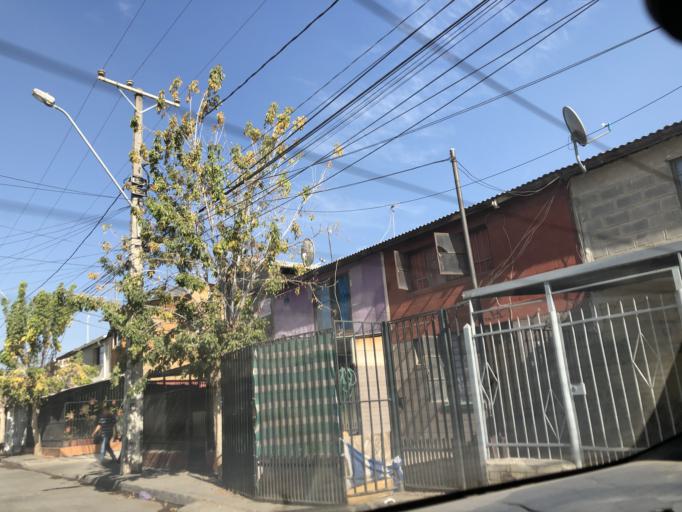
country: CL
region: Santiago Metropolitan
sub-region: Provincia de Santiago
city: La Pintana
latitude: -33.5897
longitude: -70.6025
